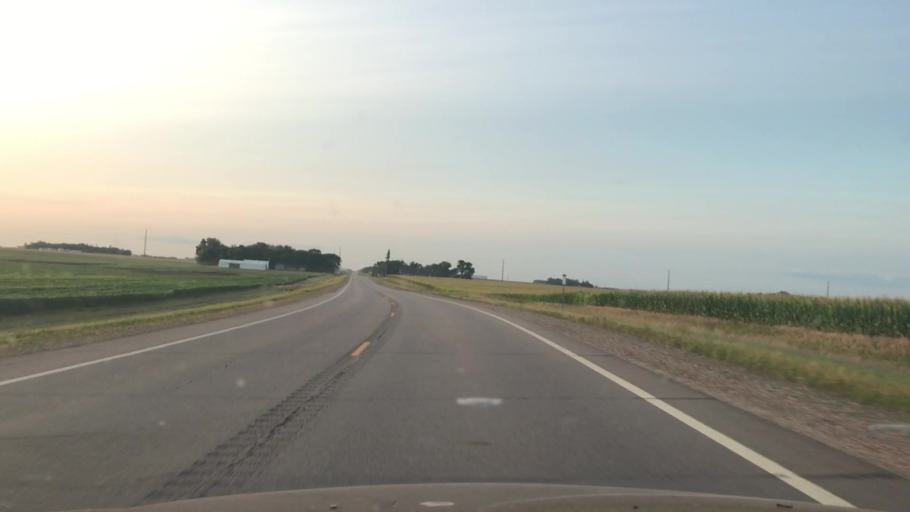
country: US
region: Minnesota
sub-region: Redwood County
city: Redwood Falls
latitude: 44.4217
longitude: -95.1176
